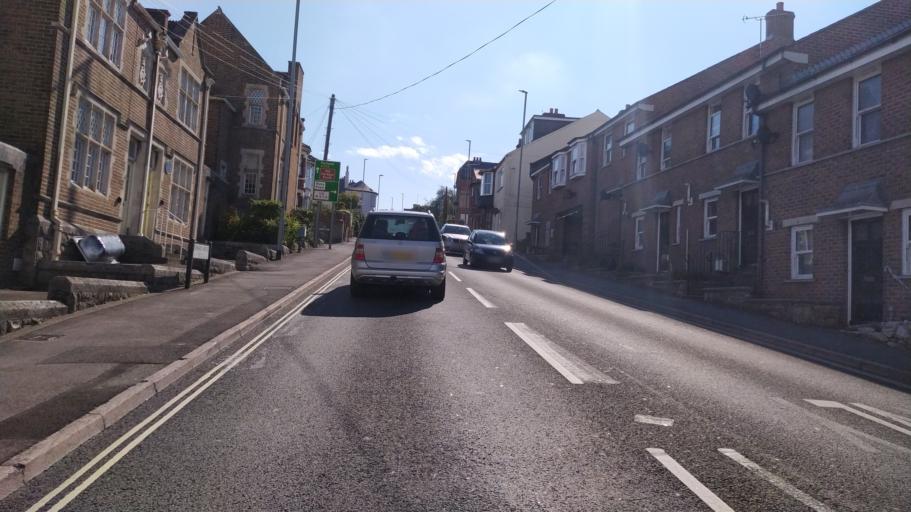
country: GB
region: England
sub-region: Dorset
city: Weymouth
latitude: 50.6062
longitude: -2.4602
